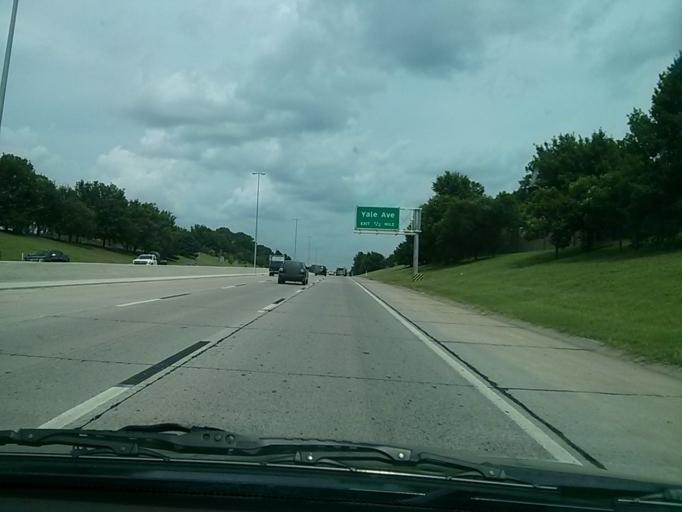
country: US
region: Oklahoma
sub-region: Tulsa County
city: Jenks
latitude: 36.0252
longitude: -95.9367
